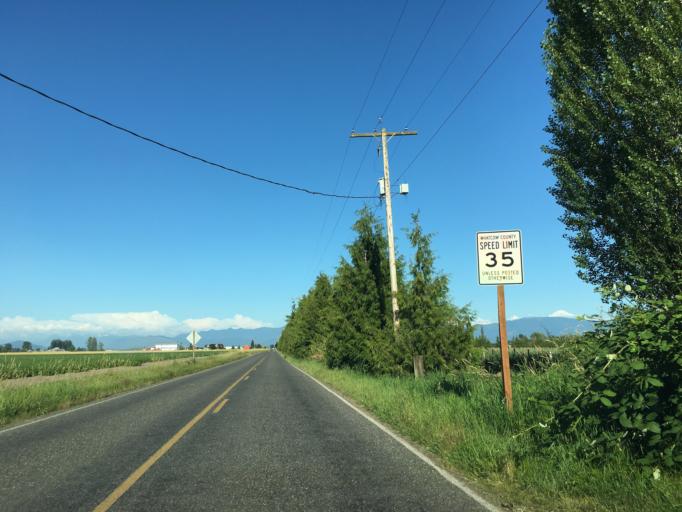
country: US
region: Washington
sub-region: Whatcom County
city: Lynden
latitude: 48.9859
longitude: -122.4840
